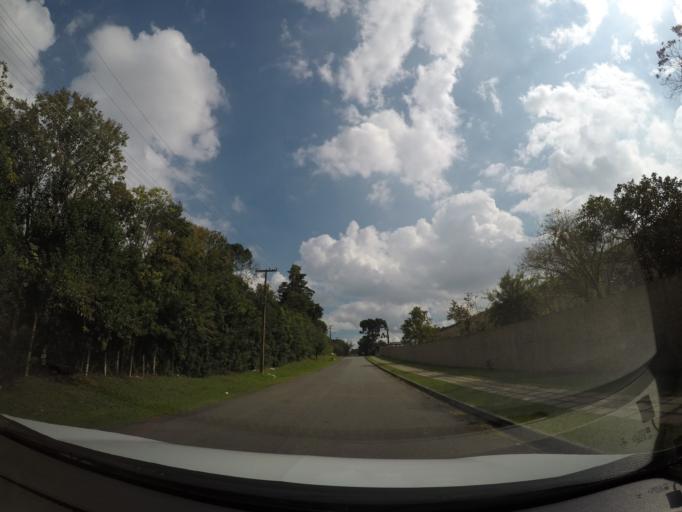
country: BR
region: Parana
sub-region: Curitiba
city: Curitiba
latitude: -25.4851
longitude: -49.2610
